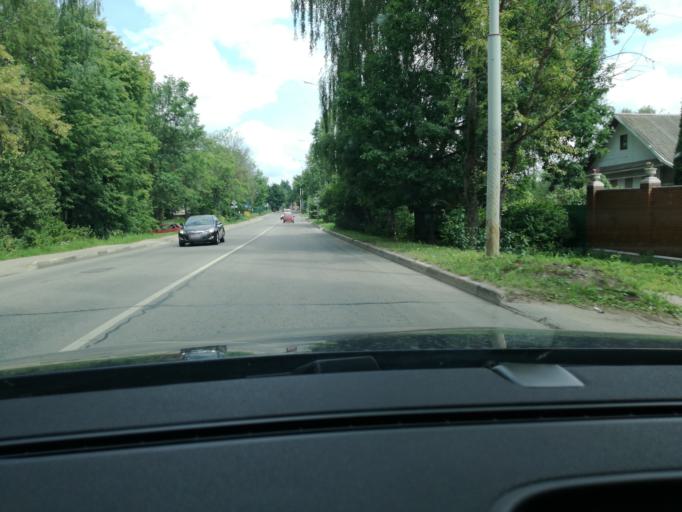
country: RU
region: Moskovskaya
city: Sergiyev Posad
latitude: 56.2926
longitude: 38.1095
